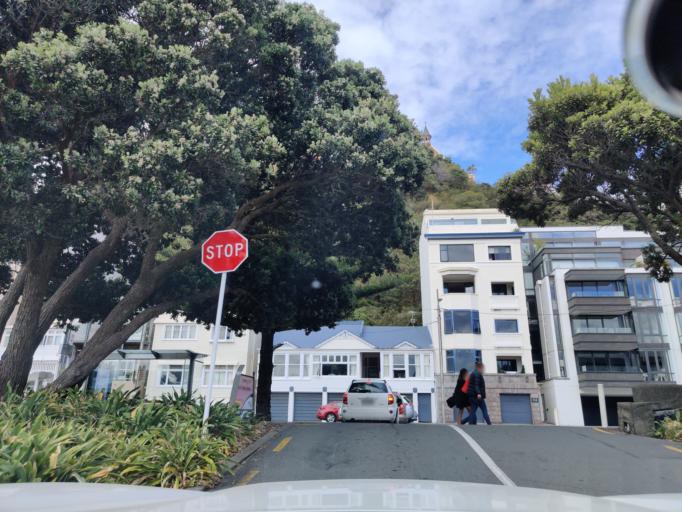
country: NZ
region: Wellington
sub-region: Wellington City
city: Wellington
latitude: -41.2908
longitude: 174.7901
